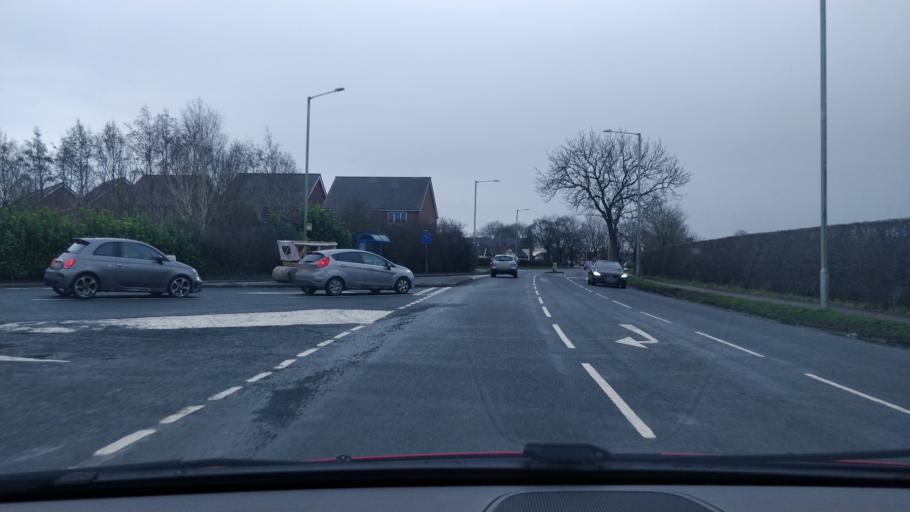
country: GB
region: England
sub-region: Lancashire
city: Tarleton
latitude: 53.7093
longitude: -2.7930
